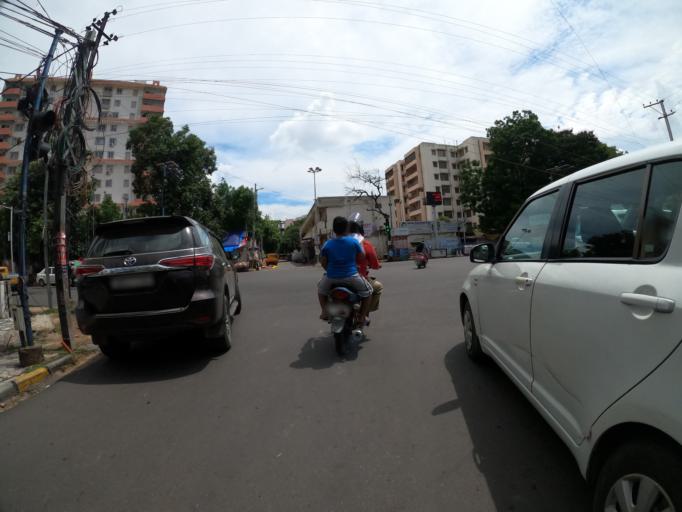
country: IN
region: Telangana
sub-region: Hyderabad
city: Hyderabad
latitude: 17.3976
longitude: 78.4838
